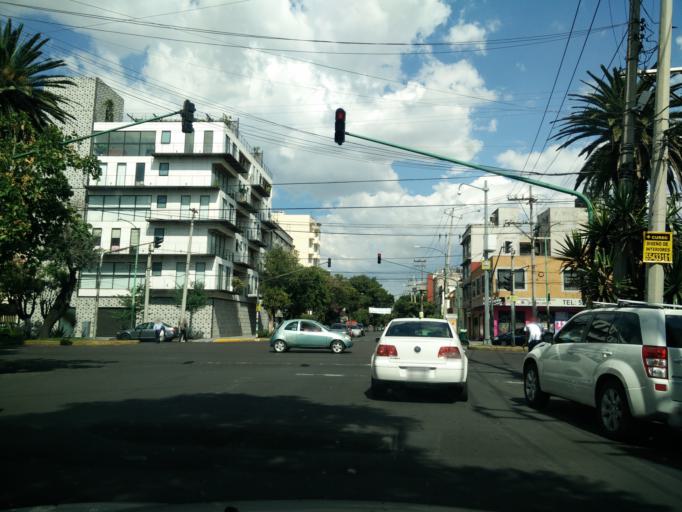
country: MX
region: Mexico City
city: Colonia del Valle
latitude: 19.3787
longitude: -99.1537
